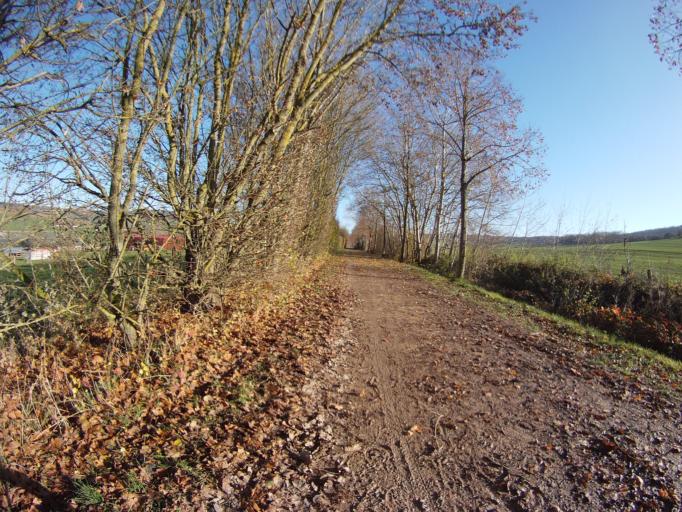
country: FR
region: Lorraine
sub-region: Departement de Meurthe-et-Moselle
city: Faulx
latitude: 48.7921
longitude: 6.2086
